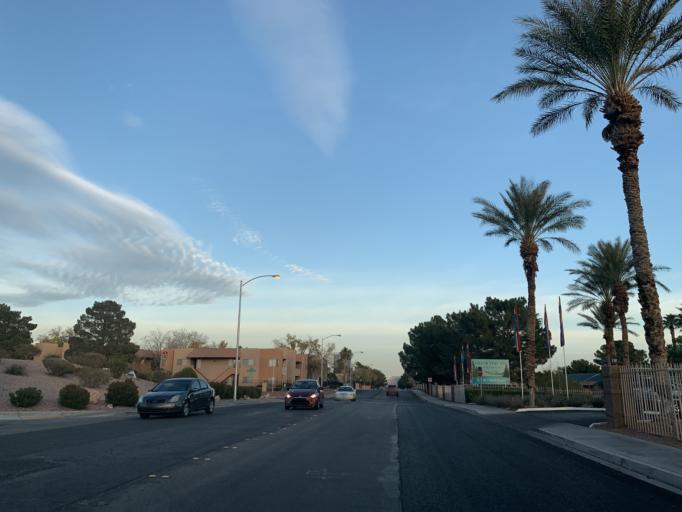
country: US
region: Nevada
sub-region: Clark County
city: Spring Valley
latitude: 36.1110
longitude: -115.2215
